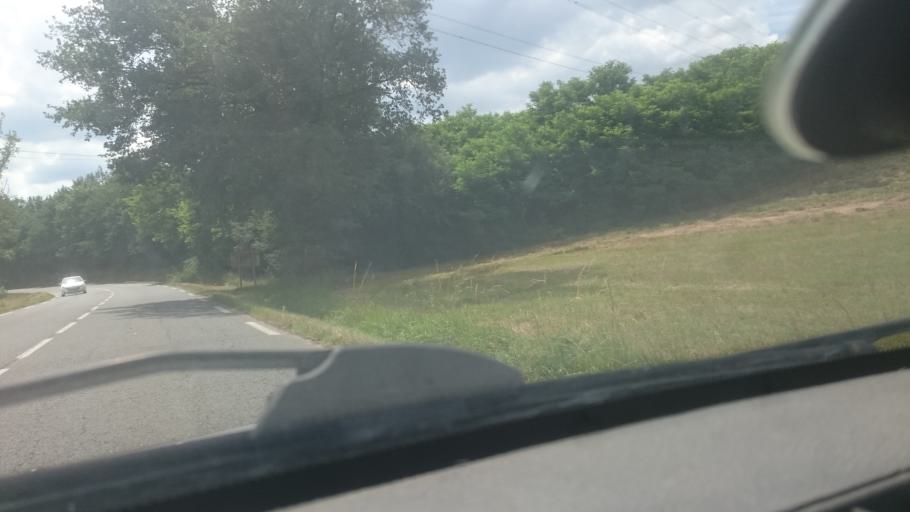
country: FR
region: Rhone-Alpes
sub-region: Departement du Rhone
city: Lozanne
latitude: 45.8575
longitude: 4.6543
